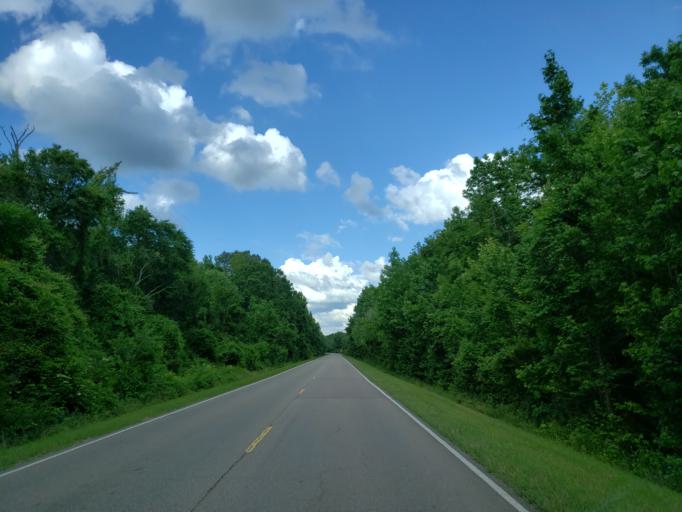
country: US
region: Mississippi
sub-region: Forrest County
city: Petal
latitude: 31.2619
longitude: -89.2222
